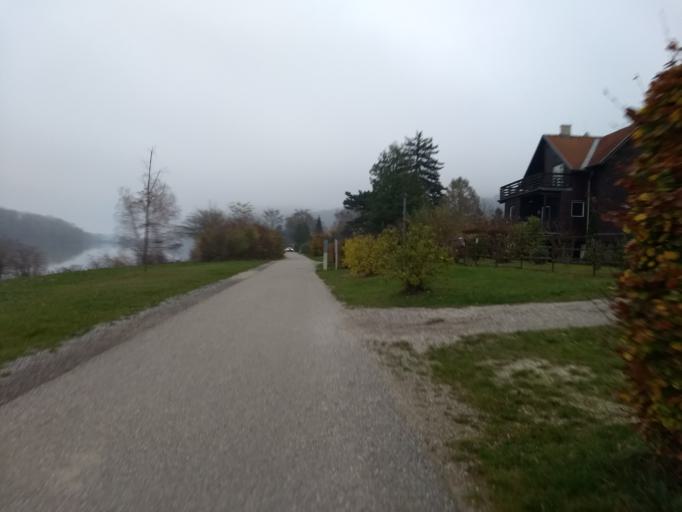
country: AT
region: Lower Austria
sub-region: Politischer Bezirk Tulln
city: Wordern
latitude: 48.3447
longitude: 16.2288
